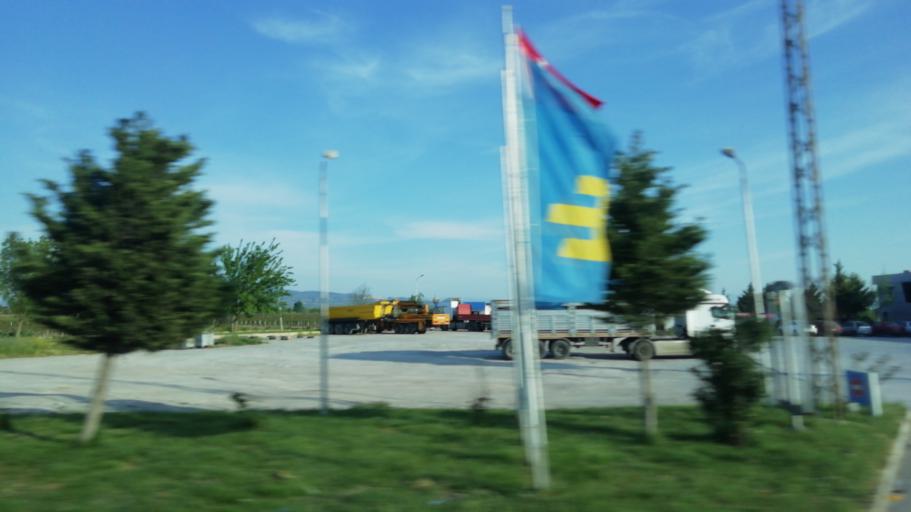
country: TR
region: Manisa
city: Saruhanli
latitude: 38.7331
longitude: 27.5873
